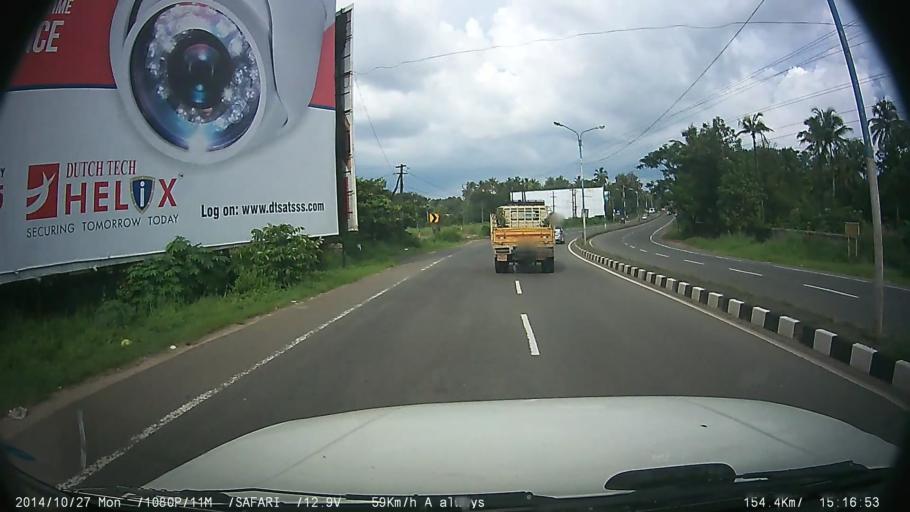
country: IN
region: Kerala
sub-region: Ernakulam
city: Aluva
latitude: 10.1604
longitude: 76.3612
